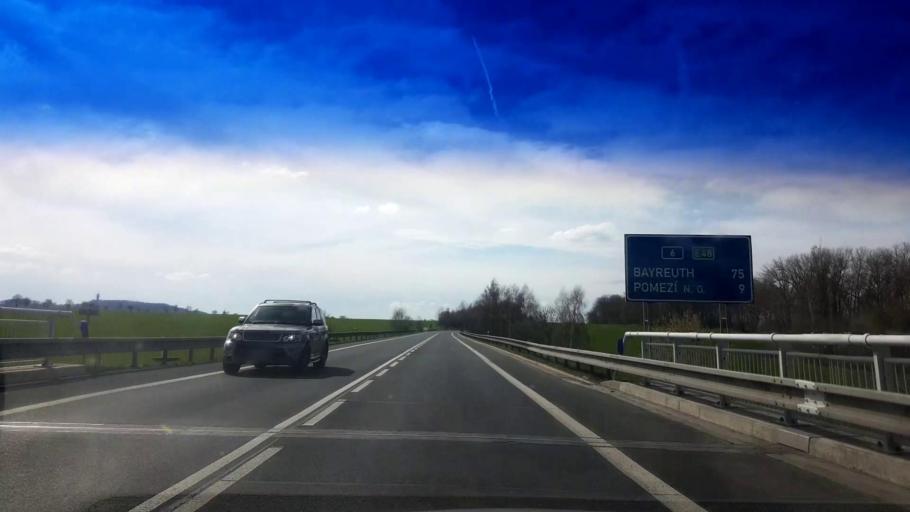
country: CZ
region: Karlovarsky
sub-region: Okres Cheb
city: Cheb
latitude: 50.0959
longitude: 12.3579
